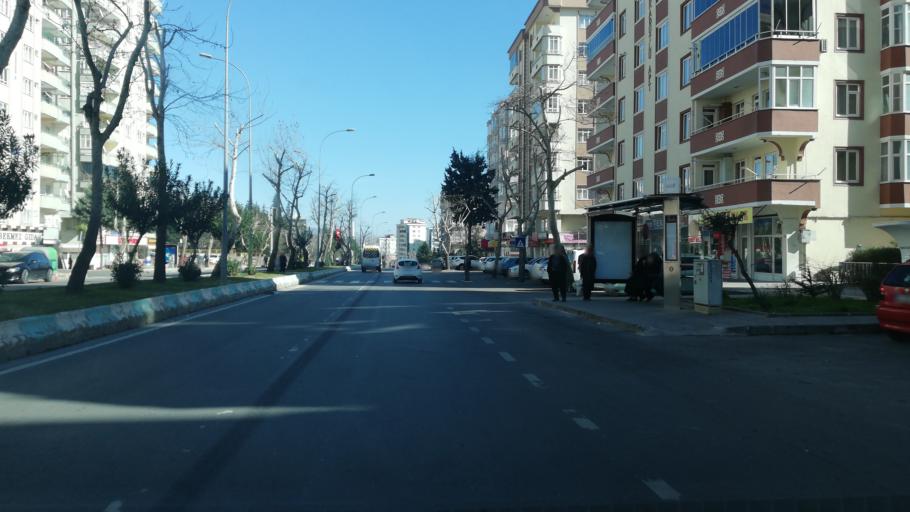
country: TR
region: Kahramanmaras
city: Kahramanmaras
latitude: 37.5867
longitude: 36.8995
